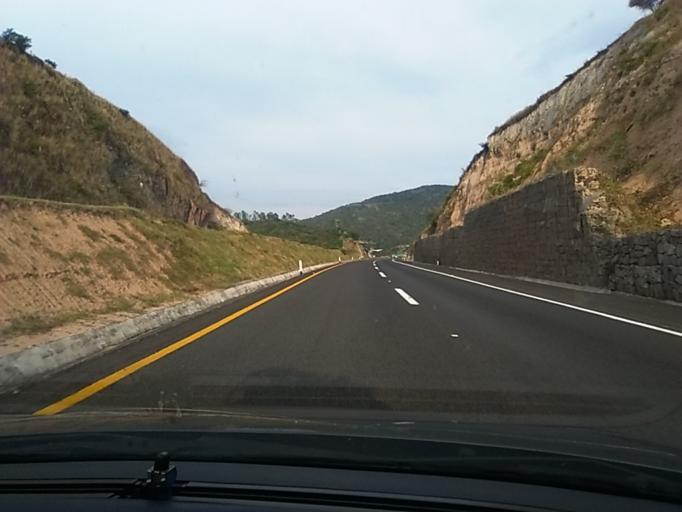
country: MX
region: Michoacan
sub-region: Cuitzeo
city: San Juan Benito Juarez (San Juan Tararameo)
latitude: 19.8931
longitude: -101.1604
